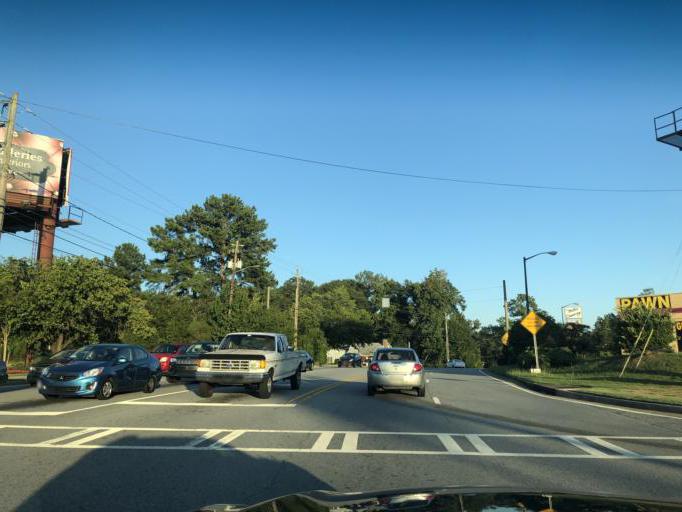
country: US
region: Georgia
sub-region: Muscogee County
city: Columbus
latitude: 32.5222
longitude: -84.8884
